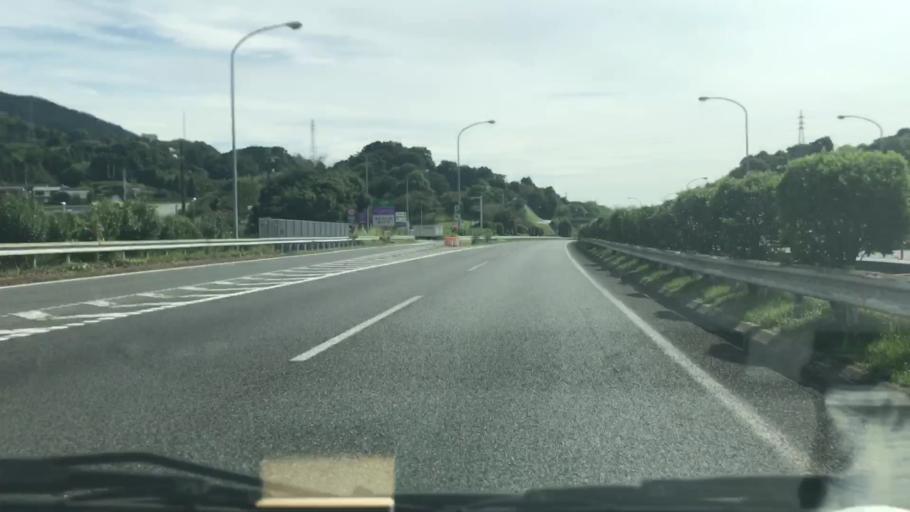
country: JP
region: Saga Prefecture
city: Saga-shi
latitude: 33.3108
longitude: 130.2061
